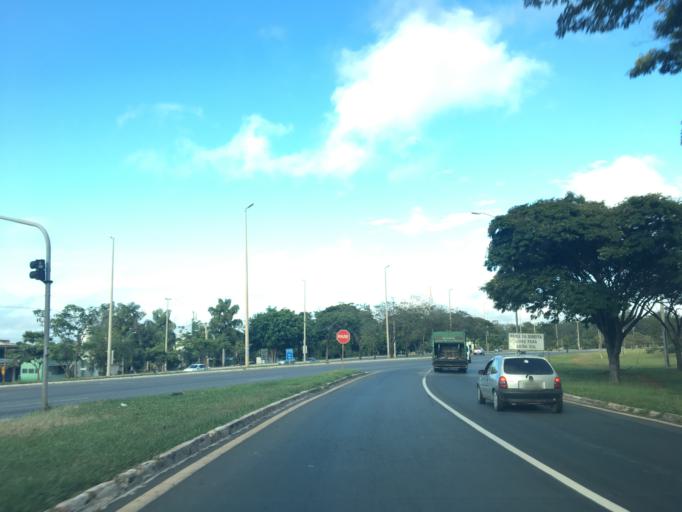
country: BR
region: Federal District
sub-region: Brasilia
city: Brasilia
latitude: -15.8445
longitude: -47.9210
